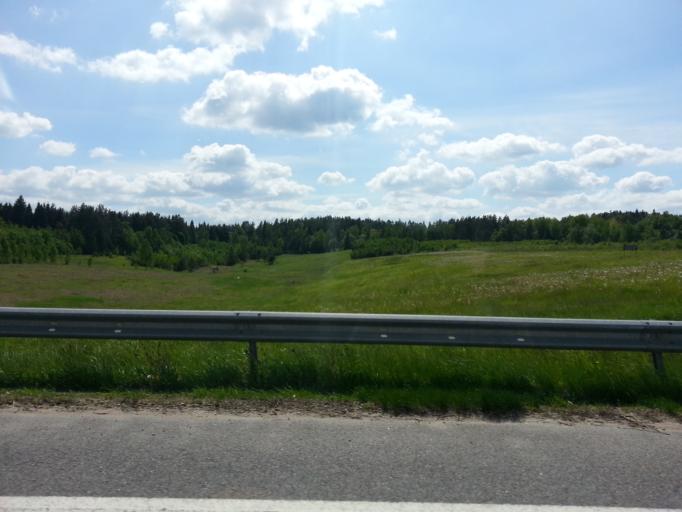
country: LT
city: Lentvaris
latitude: 54.7103
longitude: 24.9900
